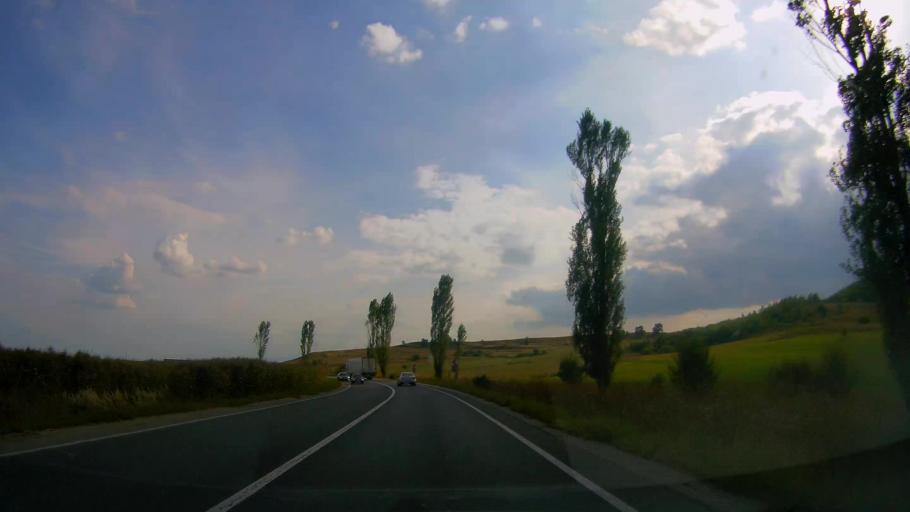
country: RO
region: Brasov
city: Maierus
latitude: 45.8856
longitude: 25.5354
